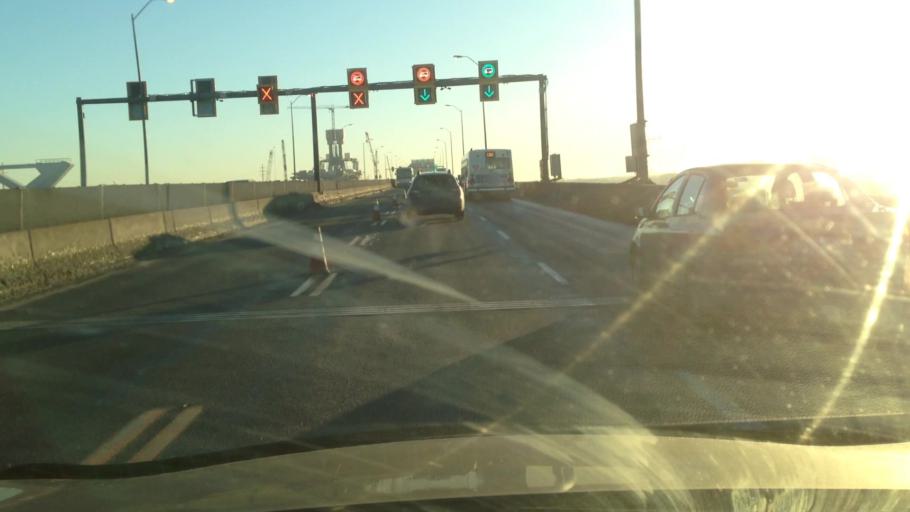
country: CA
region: Quebec
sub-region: Monteregie
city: La Prairie
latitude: 45.4686
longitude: -73.5203
